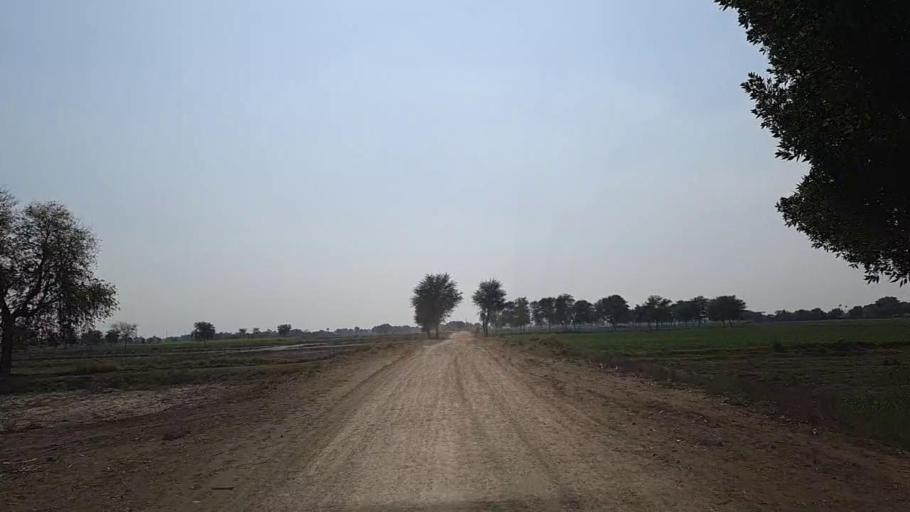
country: PK
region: Sindh
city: Nawabshah
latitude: 26.2612
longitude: 68.4901
